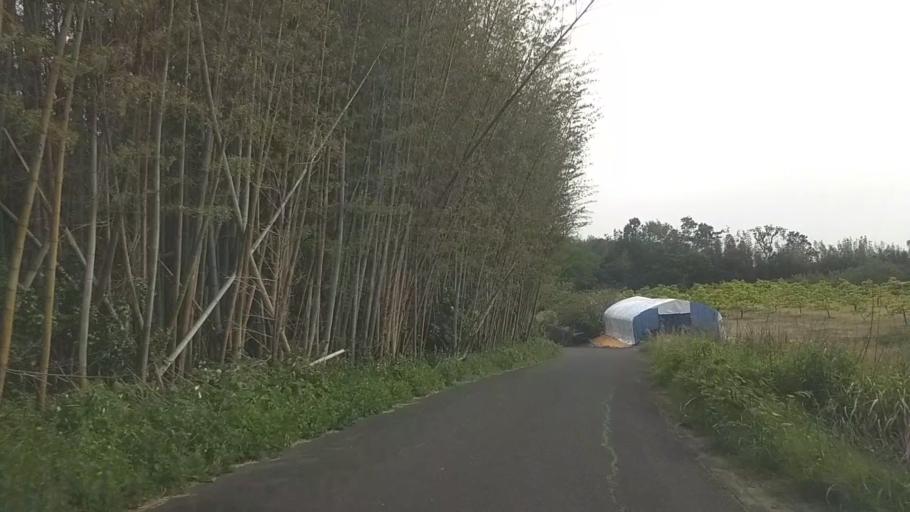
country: JP
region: Shizuoka
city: Hamamatsu
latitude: 34.7265
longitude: 137.6348
